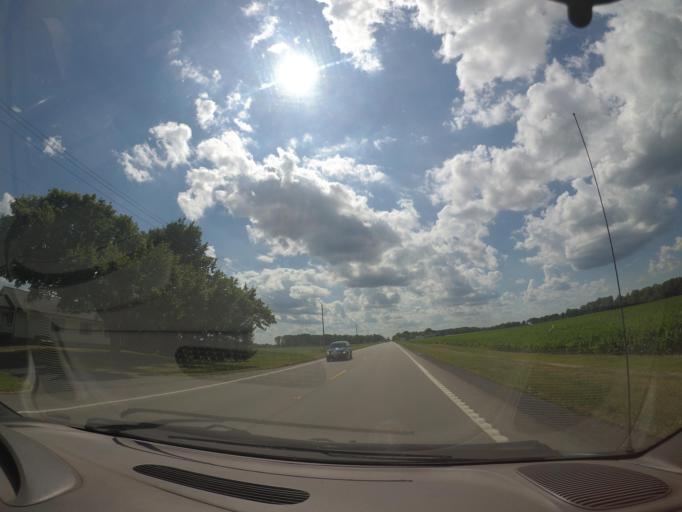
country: US
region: Ohio
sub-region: Huron County
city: Norwalk
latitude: 41.2493
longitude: -82.5505
